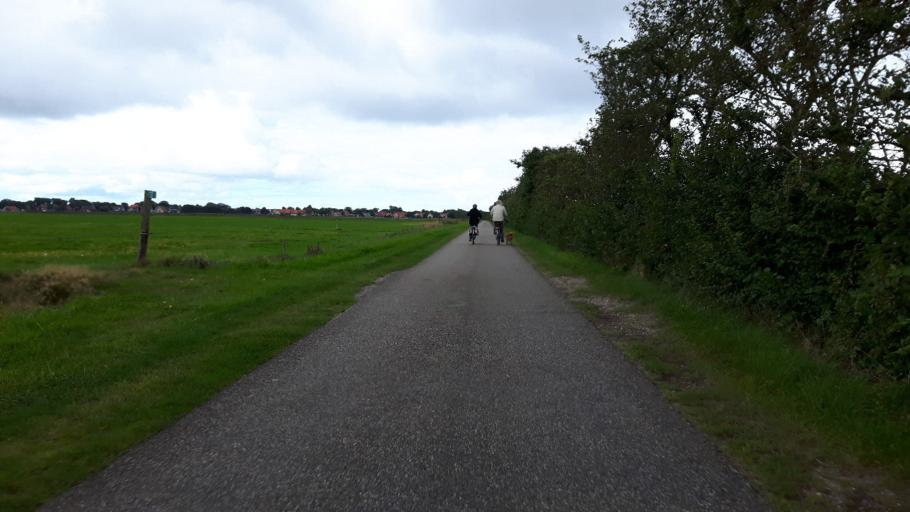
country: NL
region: Friesland
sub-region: Gemeente Ameland
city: Hollum
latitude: 53.4416
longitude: 5.6590
